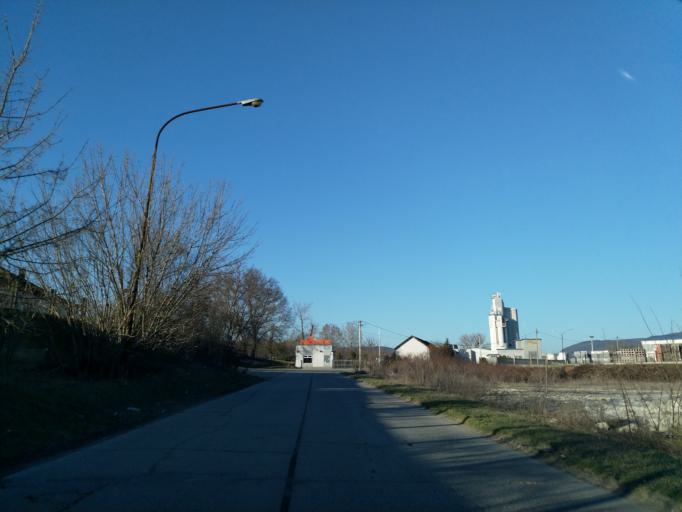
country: RS
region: Central Serbia
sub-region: Pomoravski Okrug
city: Paracin
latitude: 43.9027
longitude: 21.4955
